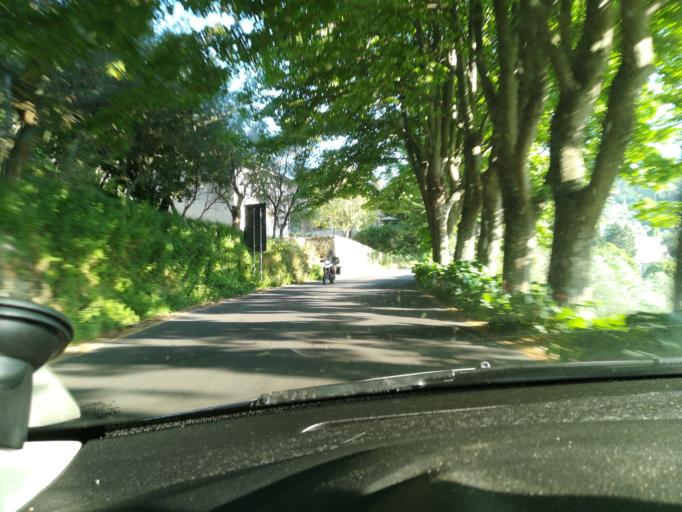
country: IT
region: Tuscany
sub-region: Provincia di Lucca
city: Stiava
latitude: 43.9123
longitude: 10.3389
